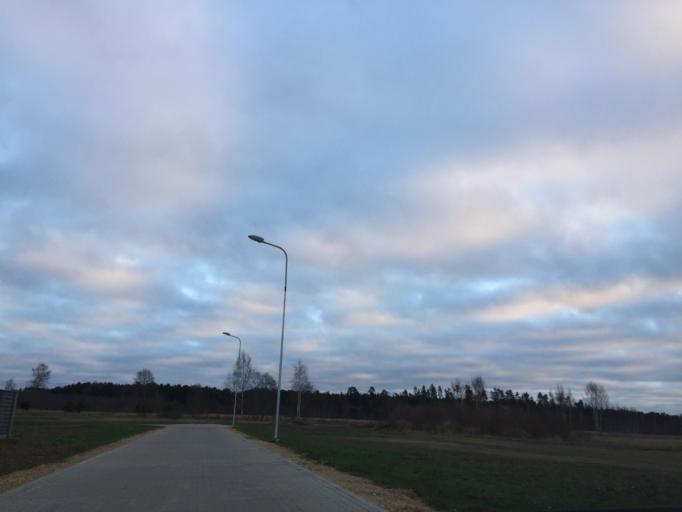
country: LV
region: Adazi
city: Adazi
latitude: 57.0664
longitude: 24.3443
